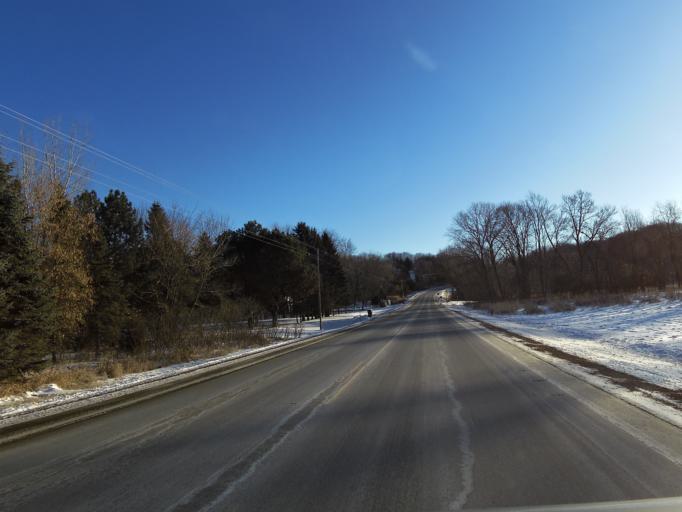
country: US
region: Minnesota
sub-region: Carver County
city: Carver
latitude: 44.7330
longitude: -93.5844
